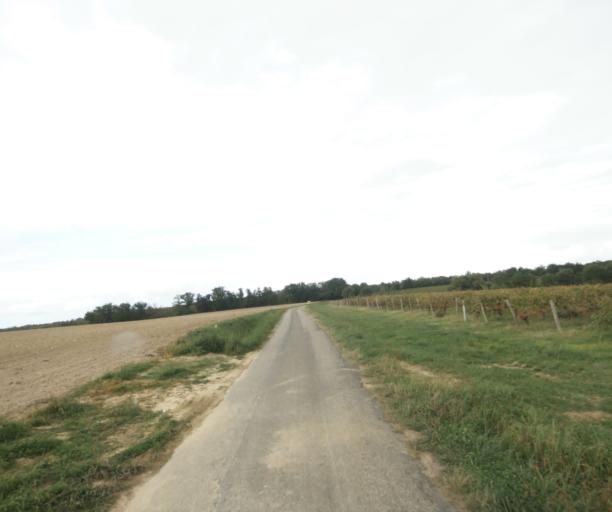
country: FR
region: Midi-Pyrenees
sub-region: Departement du Gers
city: Eauze
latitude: 43.8896
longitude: 0.1074
